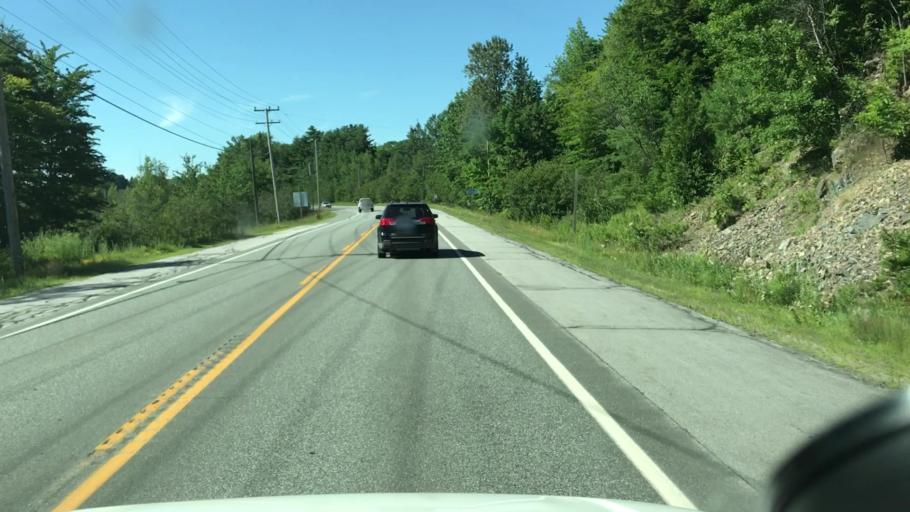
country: US
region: Maine
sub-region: Hancock County
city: Dedham
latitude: 44.7319
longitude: -68.6244
